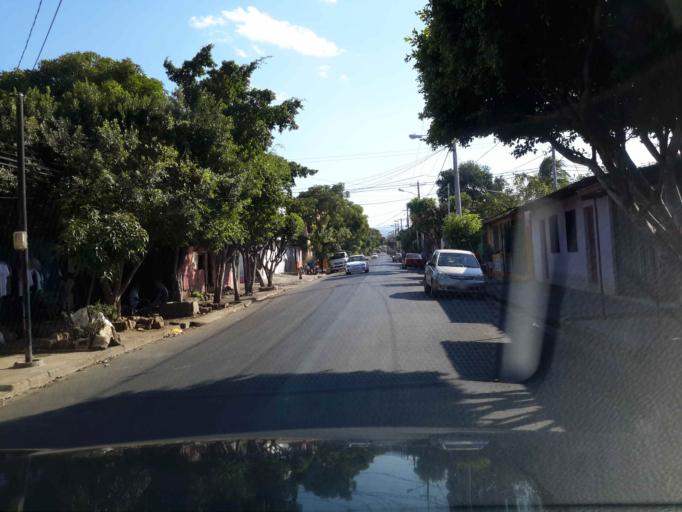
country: NI
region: Managua
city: Managua
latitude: 12.1331
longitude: -86.2525
